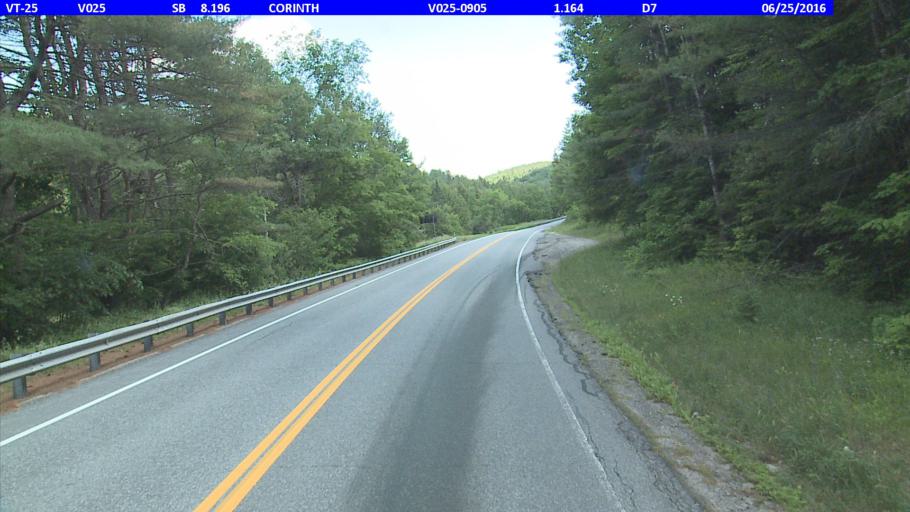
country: US
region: New Hampshire
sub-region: Grafton County
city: Haverhill
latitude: 44.0531
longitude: -72.2185
